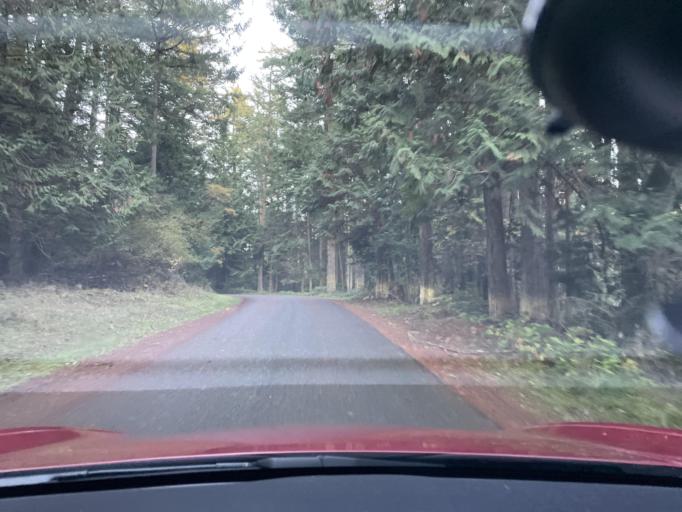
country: US
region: Washington
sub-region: San Juan County
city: Friday Harbor
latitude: 48.6197
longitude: -123.1459
